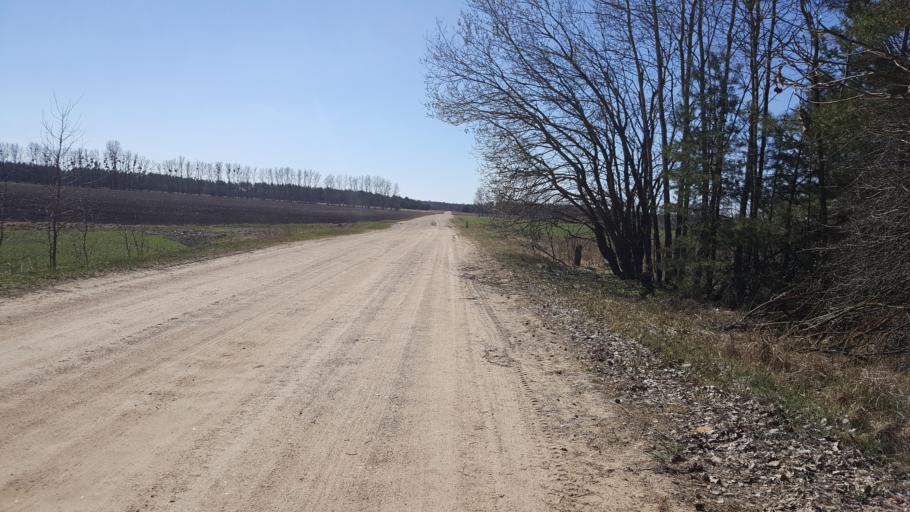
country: BY
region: Brest
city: Kamyanyets
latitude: 52.3153
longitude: 23.8624
